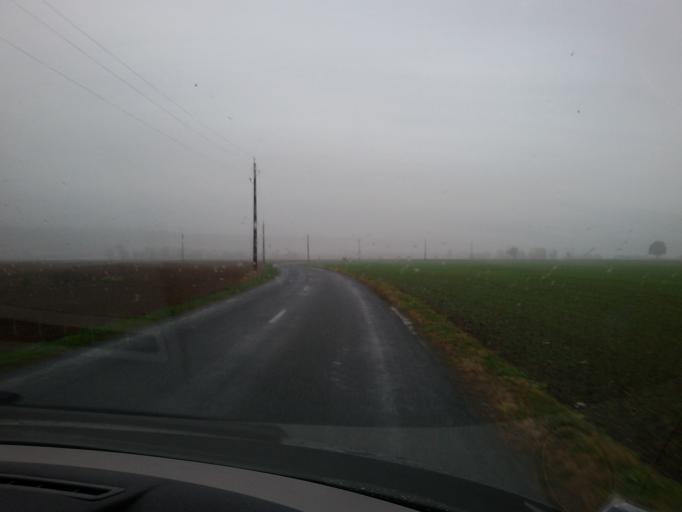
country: FR
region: Haute-Normandie
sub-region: Departement de la Seine-Maritime
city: La Cerlangue
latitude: 49.4230
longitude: 0.3841
